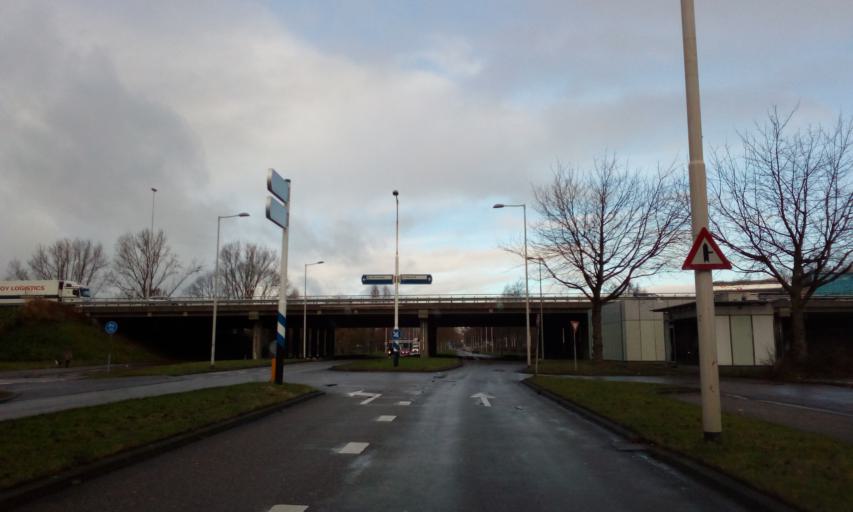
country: NL
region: South Holland
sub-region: Gemeente Rotterdam
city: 's-Gravenland
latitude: 51.9528
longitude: 4.5510
